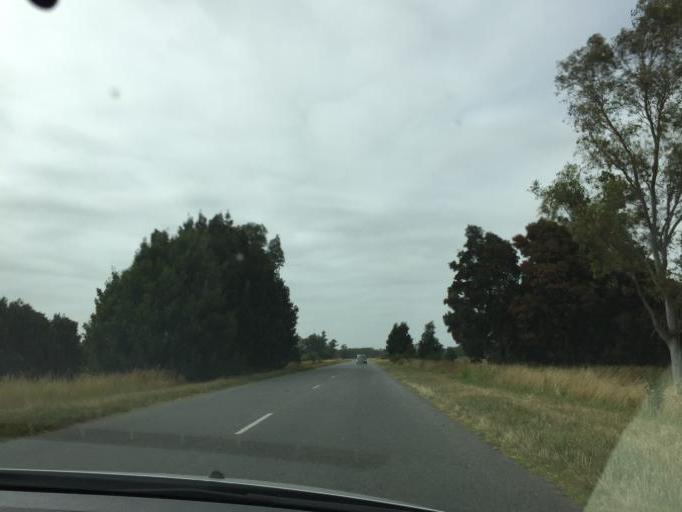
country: AR
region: Buenos Aires
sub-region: Partido de Las Flores
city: Las Flores
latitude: -36.2021
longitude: -59.0510
